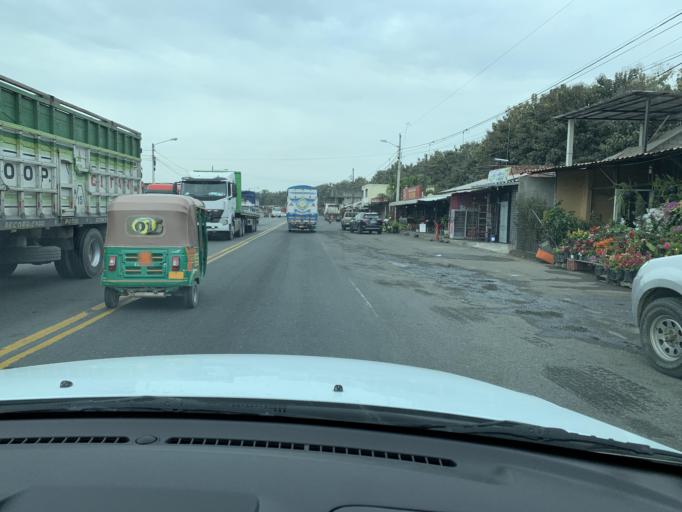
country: EC
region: Guayas
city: Yaguachi Nuevo
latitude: -2.2504
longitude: -79.6355
